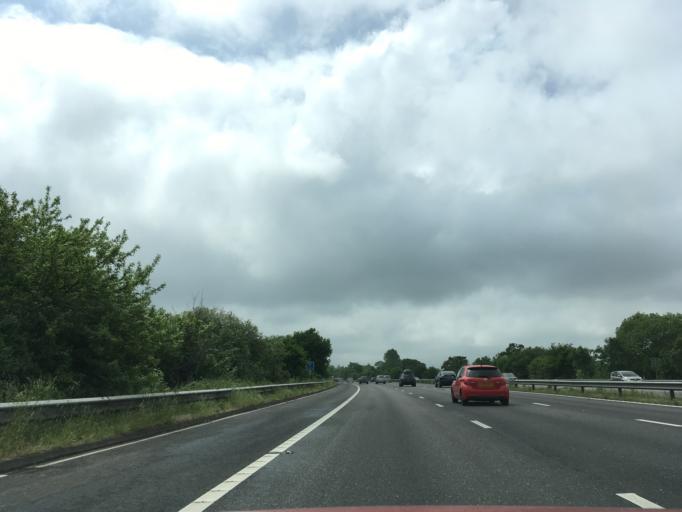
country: GB
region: England
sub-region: Devon
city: Bradninch
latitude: 50.8339
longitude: -3.3960
